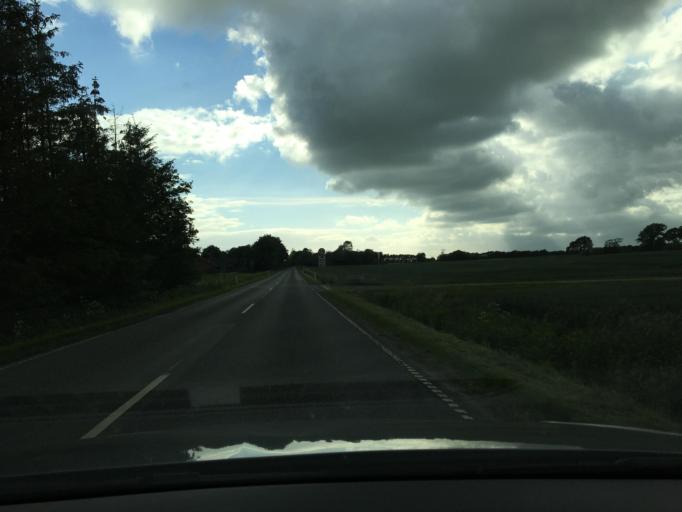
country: DK
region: Central Jutland
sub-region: Arhus Kommune
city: Hjortshoj
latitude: 56.3022
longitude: 10.2341
